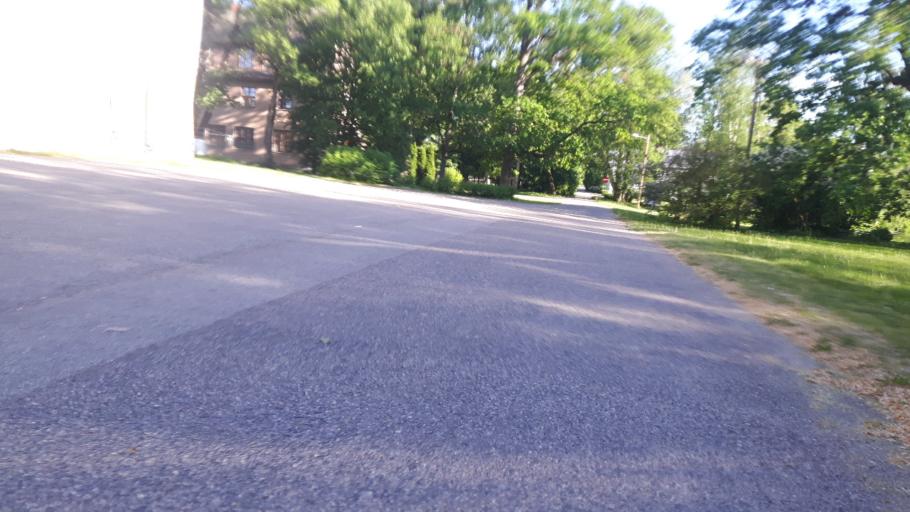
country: EE
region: Raplamaa
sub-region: Kehtna vald
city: Kehtna
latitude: 58.9229
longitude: 24.8728
